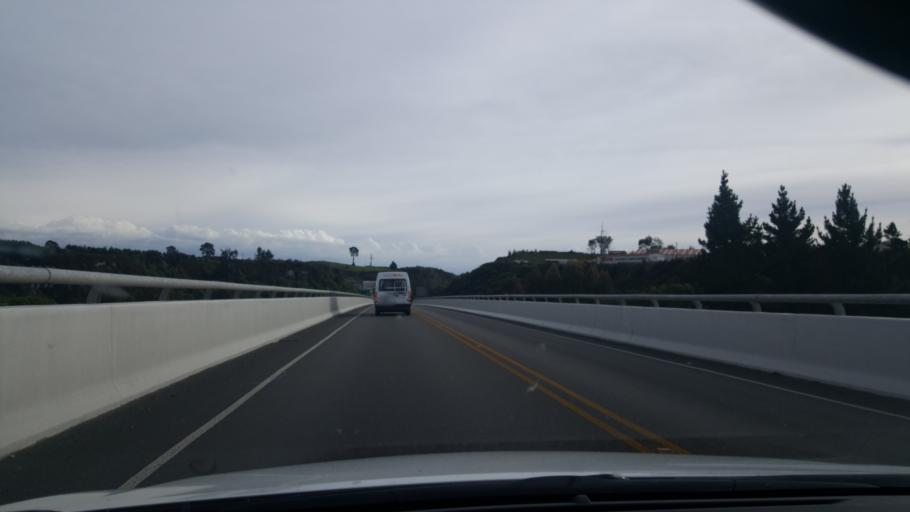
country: NZ
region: Waikato
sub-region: Taupo District
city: Taupo
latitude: -38.6269
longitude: 176.0988
